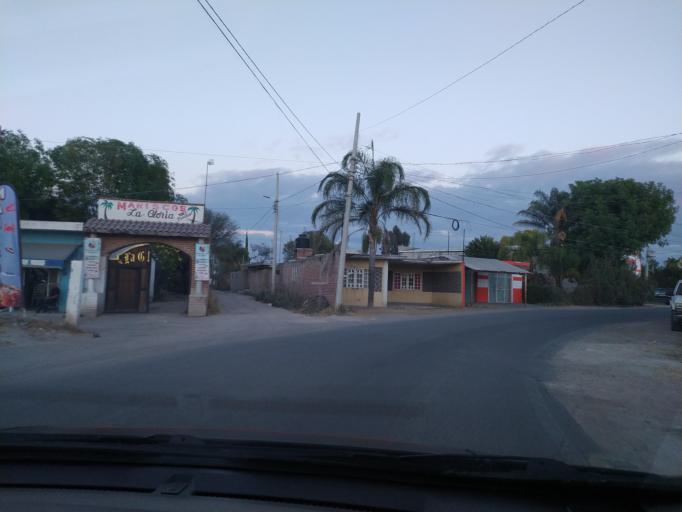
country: MX
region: Guanajuato
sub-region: San Francisco del Rincon
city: San Roque de Montes
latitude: 21.0164
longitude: -101.8167
